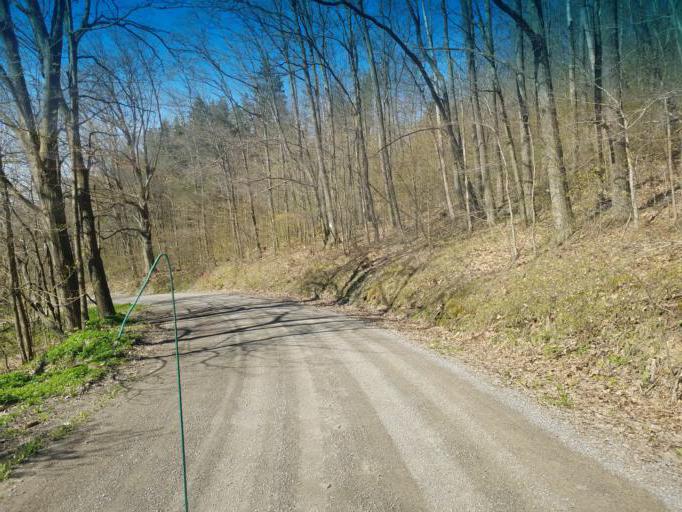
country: US
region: New York
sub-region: Allegany County
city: Andover
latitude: 41.9751
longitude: -77.7858
